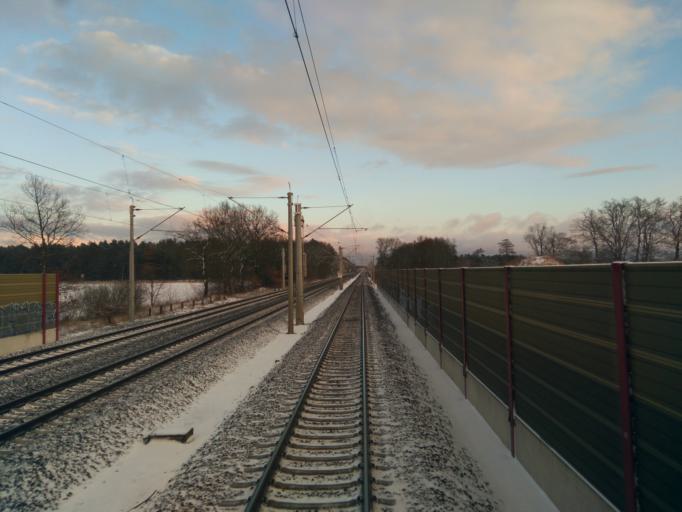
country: DE
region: Lower Saxony
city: Radbruch
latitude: 53.3161
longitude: 10.2947
